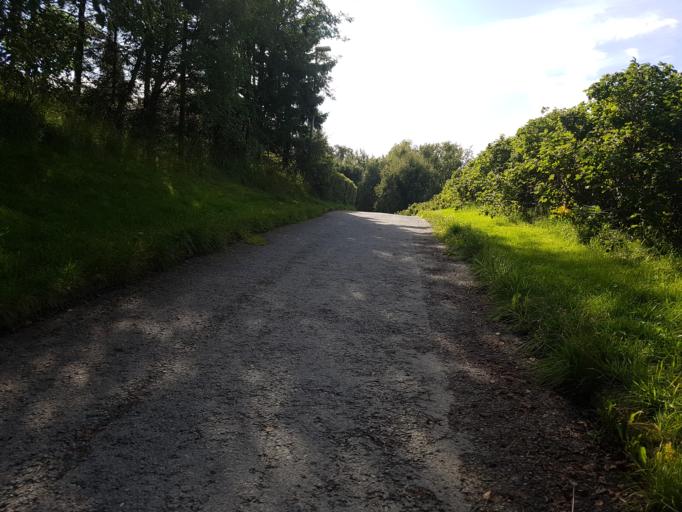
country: NO
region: Sor-Trondelag
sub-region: Trondheim
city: Trondheim
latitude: 63.4040
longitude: 10.4376
